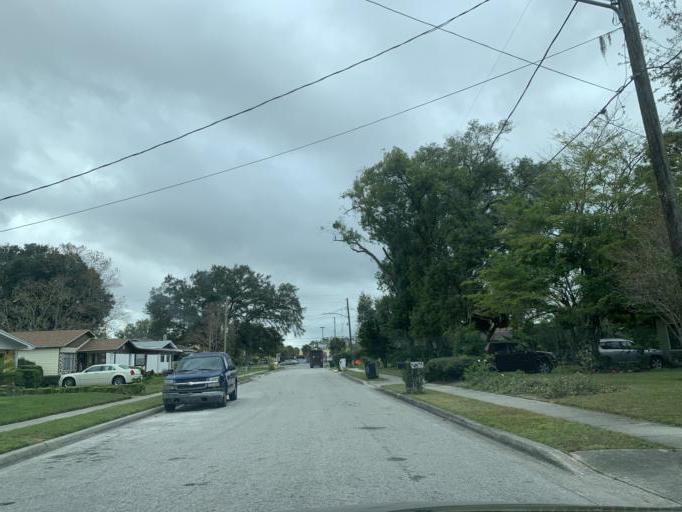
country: US
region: Florida
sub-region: Orange County
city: Eatonville
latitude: 28.6197
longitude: -81.3923
